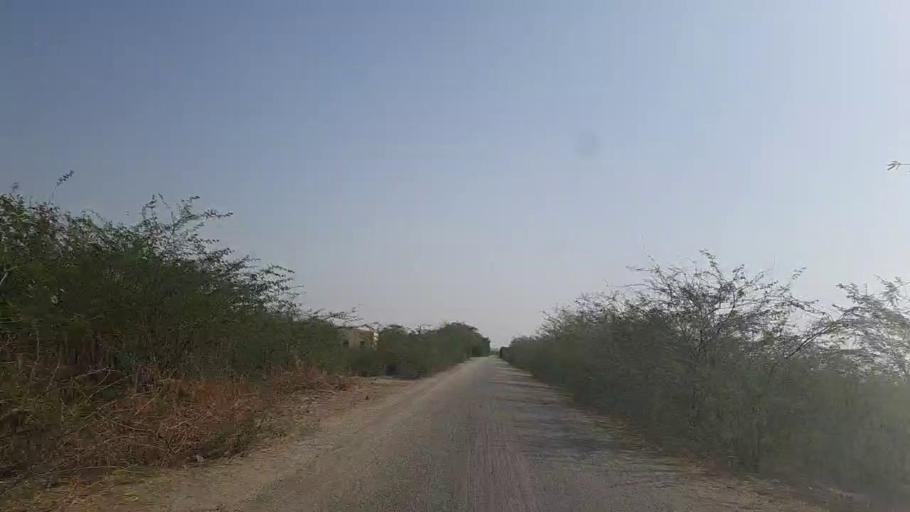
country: PK
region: Sindh
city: Kadhan
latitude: 24.5626
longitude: 69.2763
